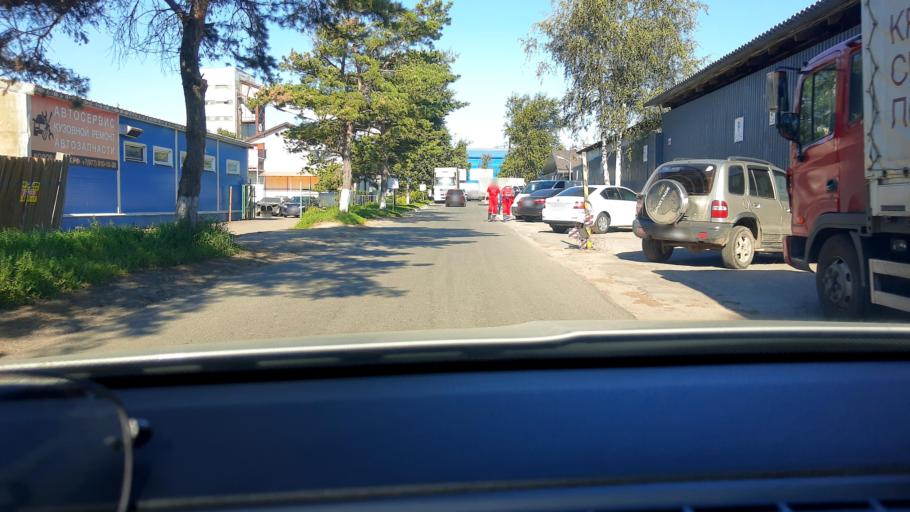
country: RU
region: Moskovskaya
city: Arkhangel'skoye
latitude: 55.8048
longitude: 37.3100
